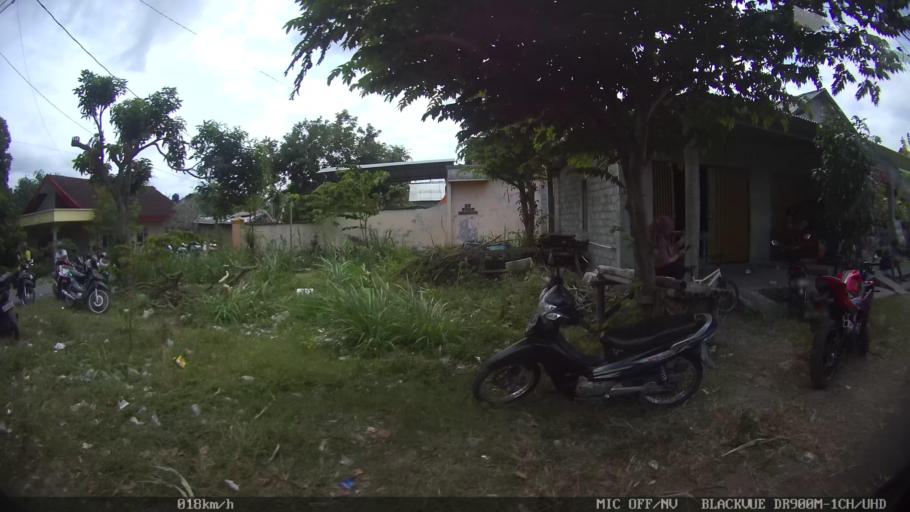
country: ID
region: Central Java
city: Candi Prambanan
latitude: -7.8147
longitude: 110.4797
